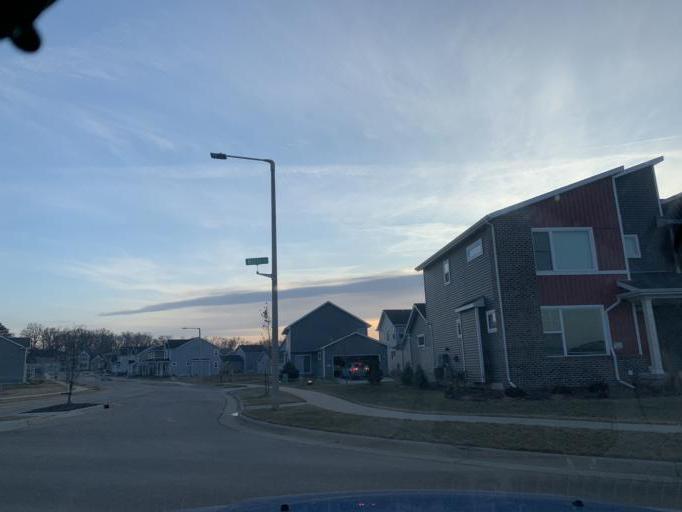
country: US
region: Wisconsin
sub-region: Dane County
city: Verona
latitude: 43.0519
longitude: -89.5552
